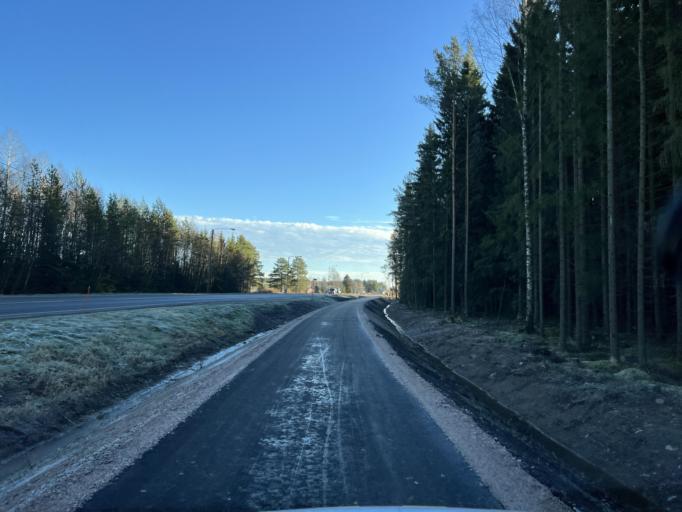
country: FI
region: Northern Ostrobothnia
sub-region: Nivala-Haapajaervi
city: Nivala
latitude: 63.9505
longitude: 24.9160
